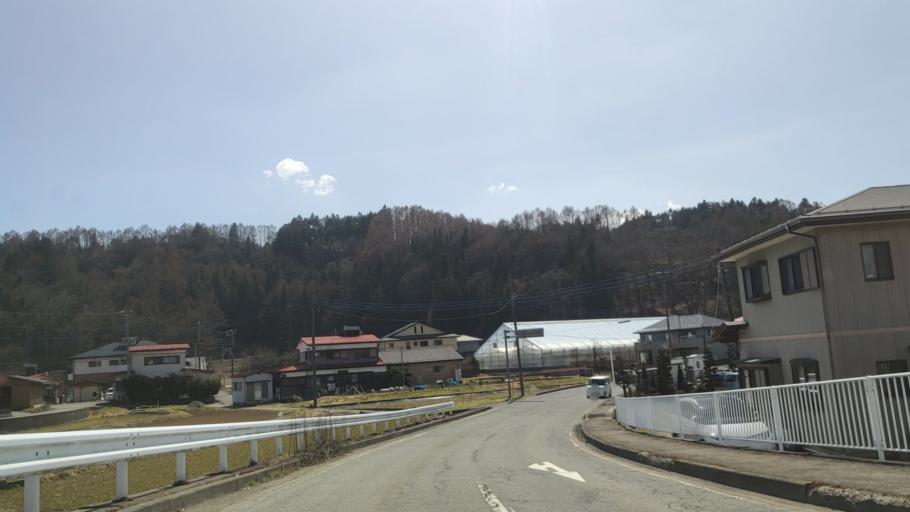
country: JP
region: Yamanashi
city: Fujikawaguchiko
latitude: 35.4933
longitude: 138.8270
